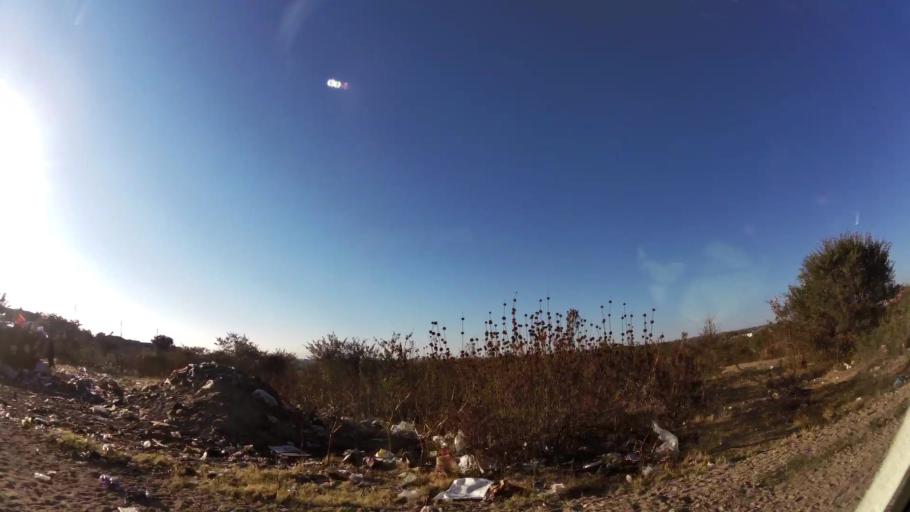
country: ZA
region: Limpopo
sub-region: Capricorn District Municipality
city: Polokwane
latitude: -23.8410
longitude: 29.3596
